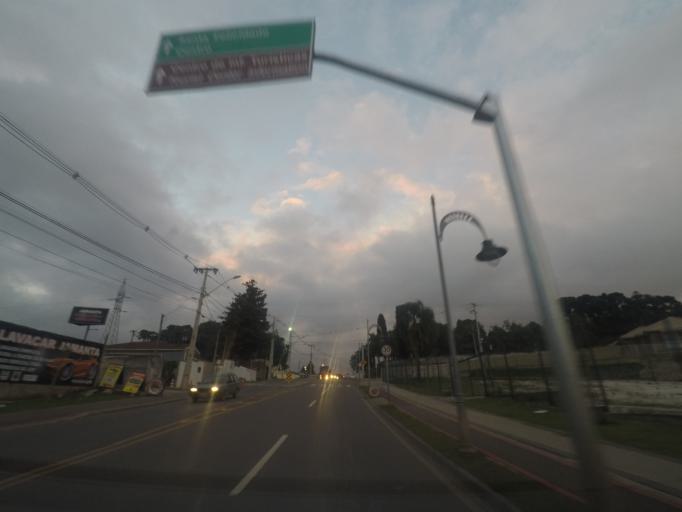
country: BR
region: Parana
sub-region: Almirante Tamandare
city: Almirante Tamandare
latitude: -25.3901
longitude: -49.3539
